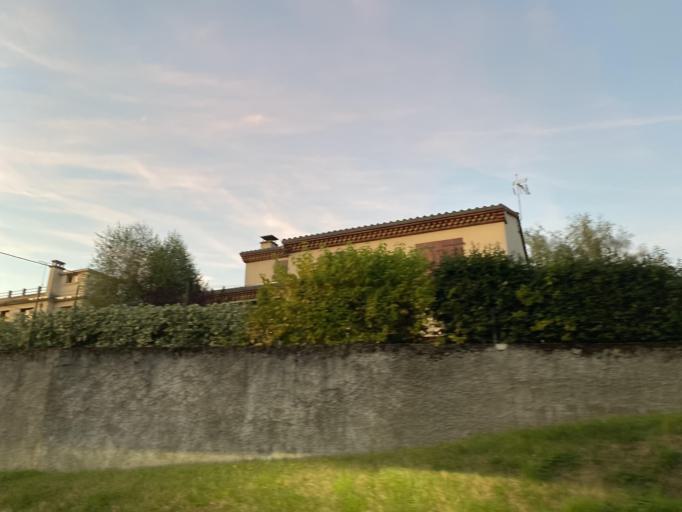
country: FR
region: Auvergne
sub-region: Departement du Puy-de-Dome
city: Ambert
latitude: 45.5448
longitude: 3.7477
